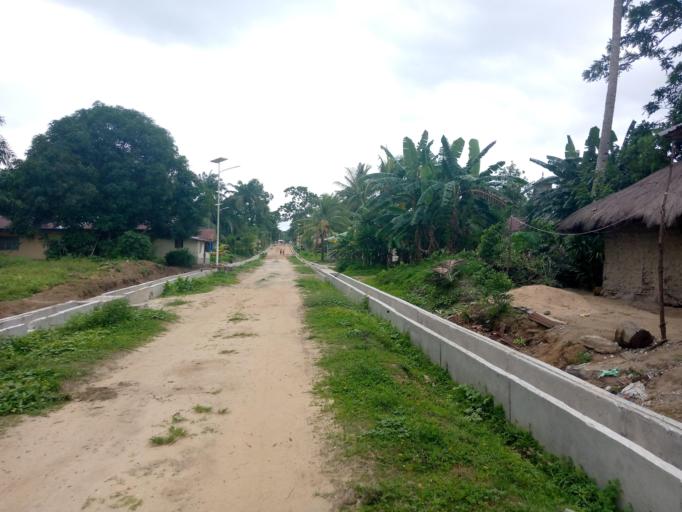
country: SL
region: Southern Province
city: Bonthe
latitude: 7.5241
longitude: -12.5067
